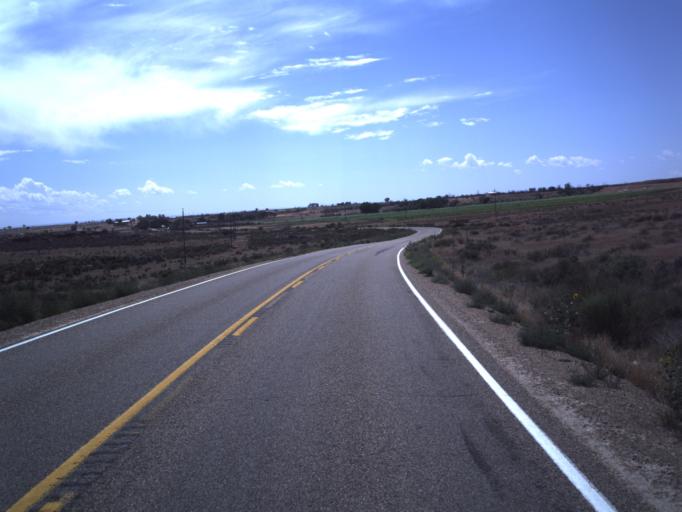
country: US
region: Utah
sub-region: Uintah County
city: Maeser
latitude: 40.2673
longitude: -109.6838
